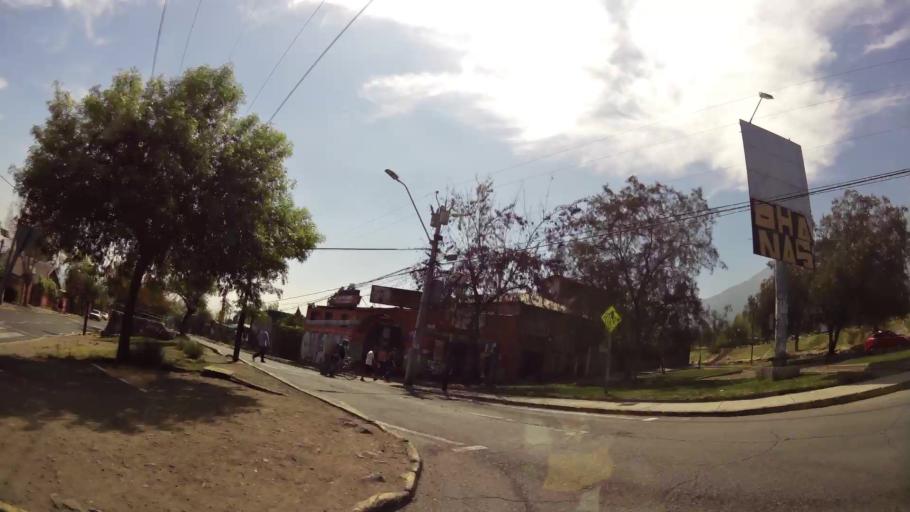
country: CL
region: Santiago Metropolitan
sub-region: Provincia de Santiago
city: Villa Presidente Frei, Nunoa, Santiago, Chile
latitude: -33.4745
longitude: -70.5267
